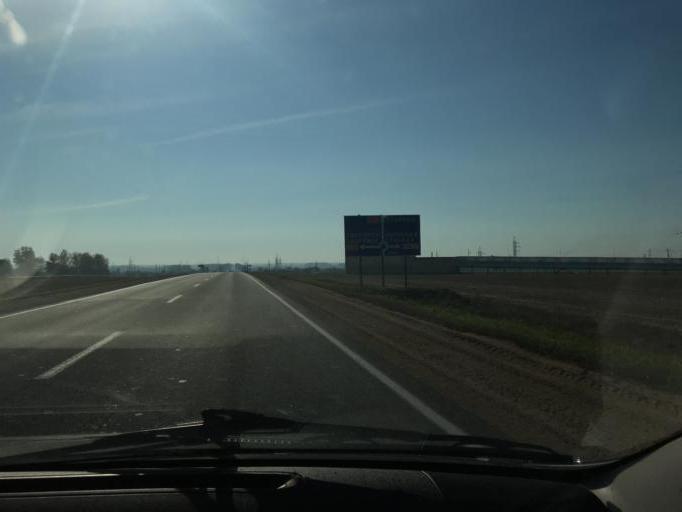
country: BY
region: Minsk
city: Salihorsk
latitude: 52.8586
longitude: 27.4668
